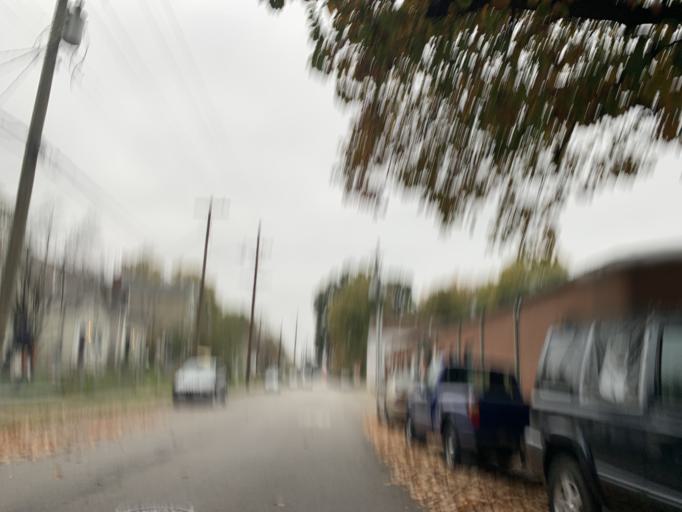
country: US
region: Kentucky
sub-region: Jefferson County
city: Louisville
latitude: 38.2617
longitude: -85.7902
